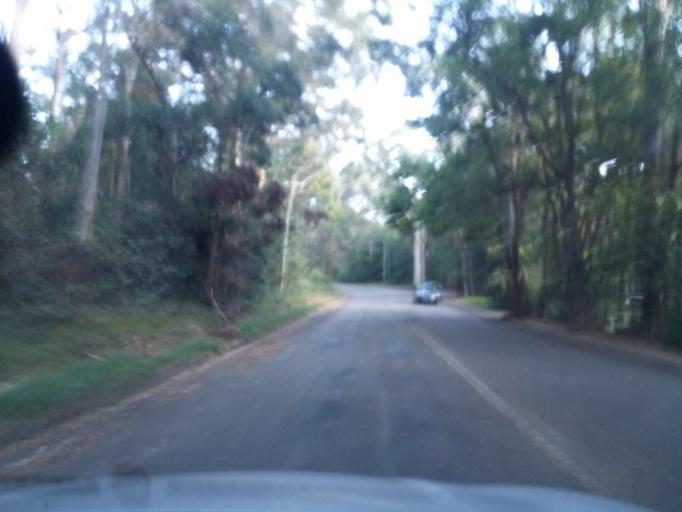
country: AU
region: New South Wales
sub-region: Port Macquarie-Hastings
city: Port Macquarie
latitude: -31.4415
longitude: 152.9181
